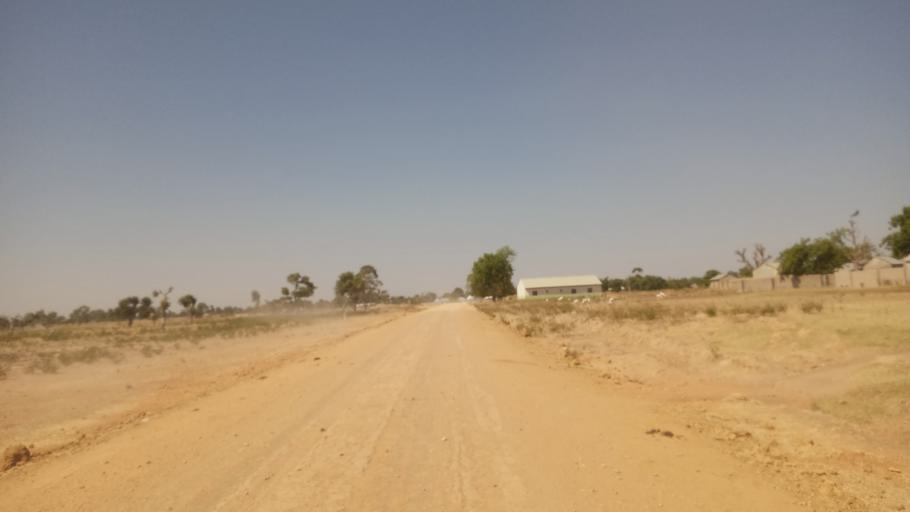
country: NG
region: Adamawa
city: Ngurore
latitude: 9.2977
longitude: 12.1410
